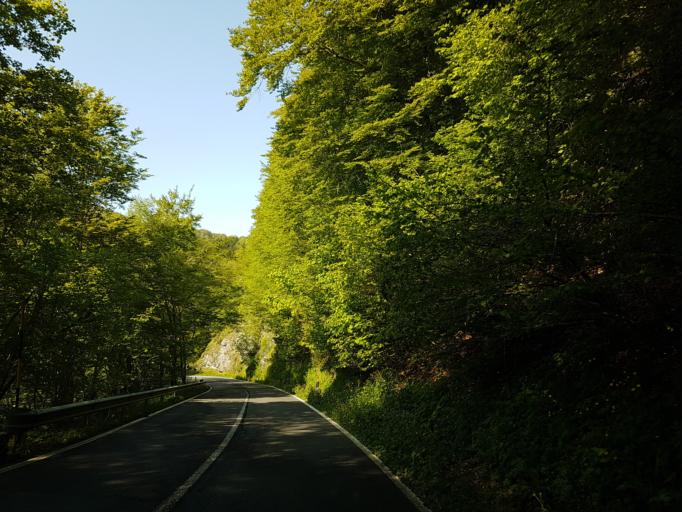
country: IT
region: Emilia-Romagna
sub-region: Forli-Cesena
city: San Piero in Bagno
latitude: 43.7963
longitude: 11.8929
